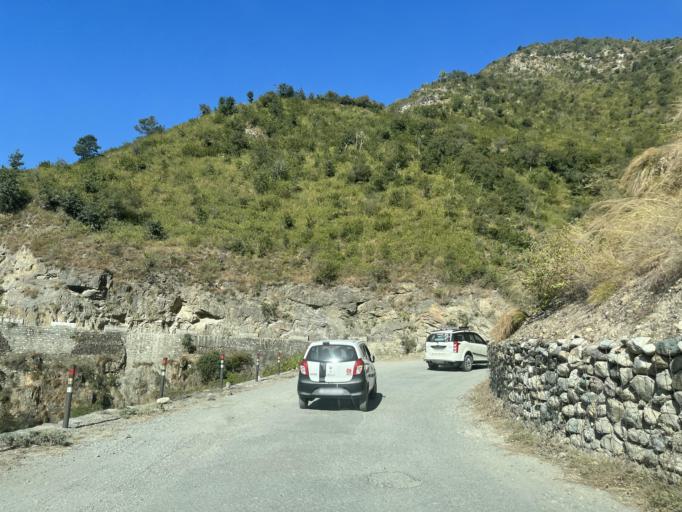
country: IN
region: Uttarakhand
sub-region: Naini Tal
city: Naini Tal
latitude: 29.5095
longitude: 79.4527
